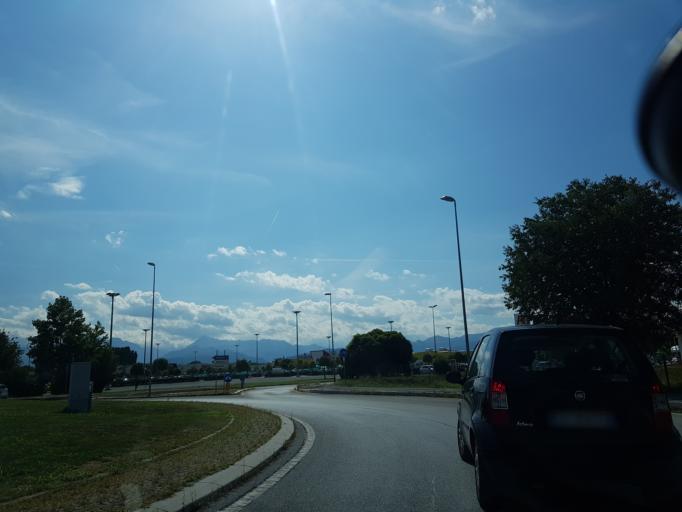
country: IT
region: Piedmont
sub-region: Provincia di Cuneo
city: Cuneo
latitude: 44.3934
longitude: 7.5863
